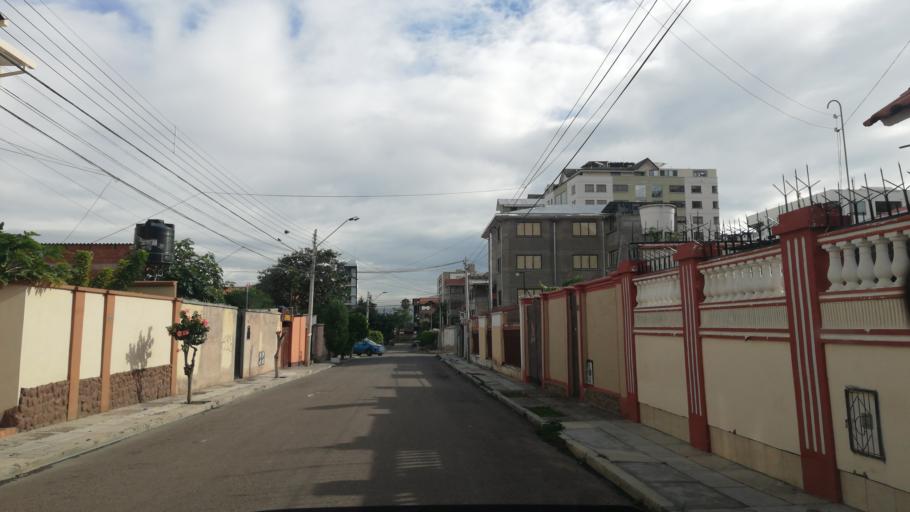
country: BO
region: Cochabamba
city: Cochabamba
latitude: -17.3743
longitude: -66.1779
